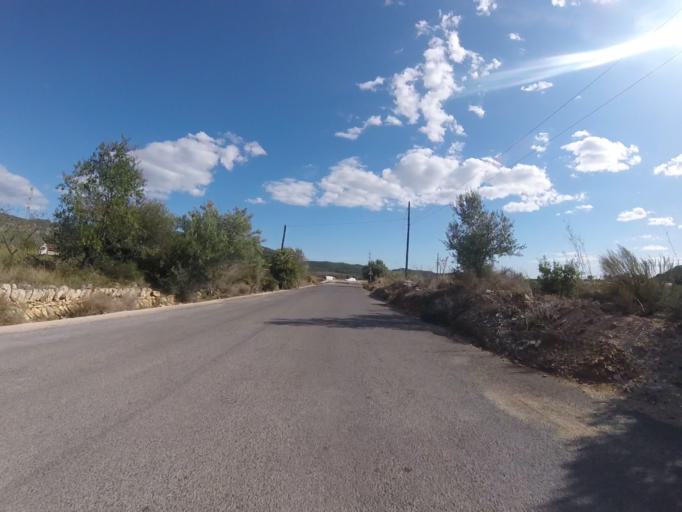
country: ES
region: Valencia
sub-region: Provincia de Castello
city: Alcala de Xivert
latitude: 40.2701
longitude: 0.2399
